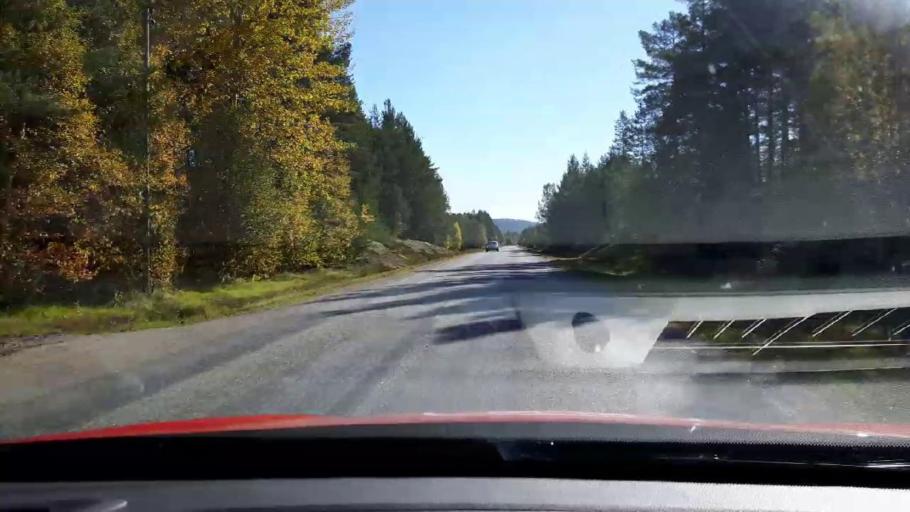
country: SE
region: Jaemtland
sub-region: Harjedalens Kommun
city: Sveg
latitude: 62.3571
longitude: 14.0134
